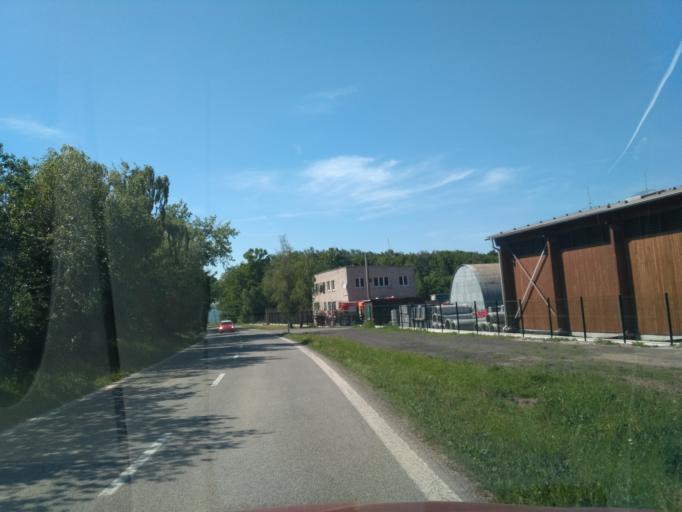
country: SK
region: Presovsky
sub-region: Okres Presov
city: Presov
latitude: 48.9415
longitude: 21.3041
